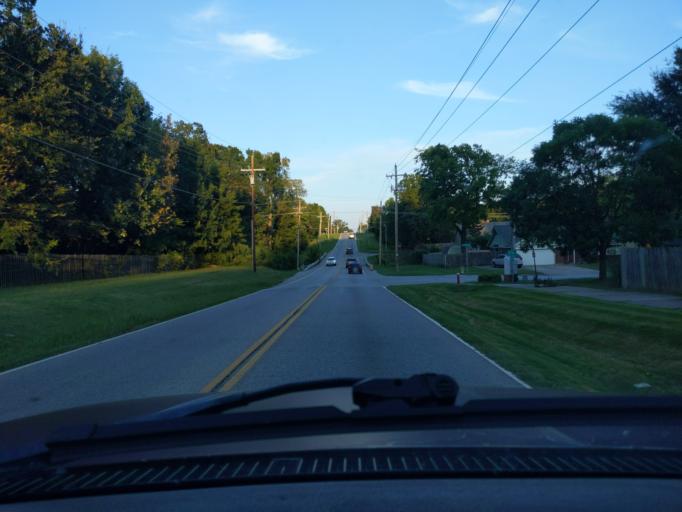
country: US
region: Oklahoma
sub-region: Tulsa County
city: Jenks
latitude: 36.0464
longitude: -95.9321
